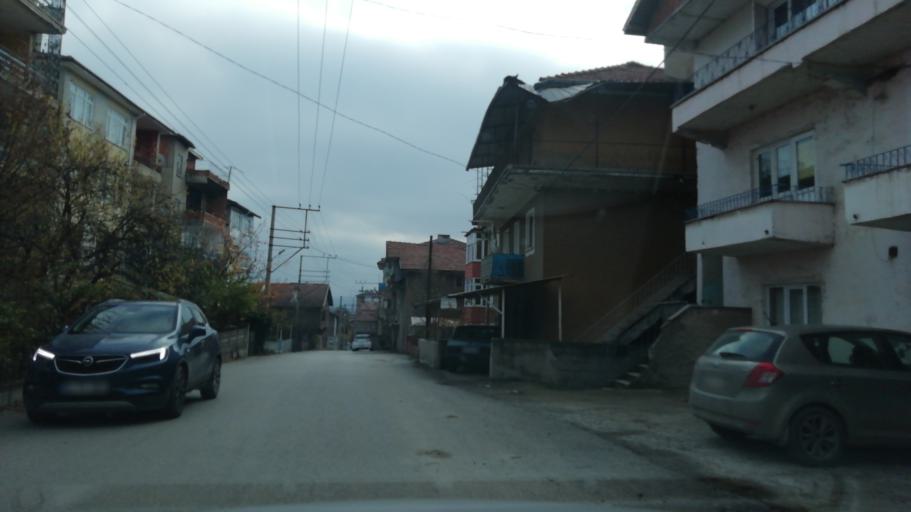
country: TR
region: Karabuk
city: Karabuk
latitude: 41.2221
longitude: 32.6267
